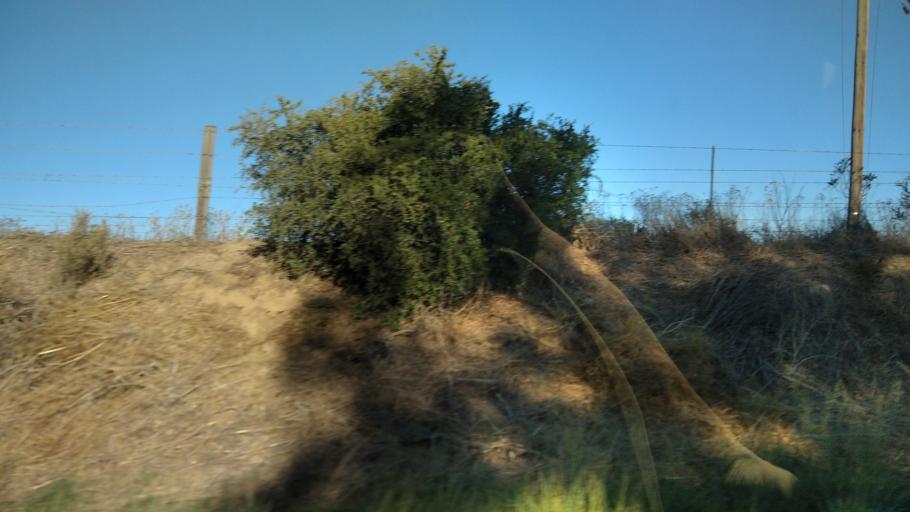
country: ZA
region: Western Cape
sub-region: West Coast District Municipality
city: Malmesbury
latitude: -33.3913
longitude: 18.6722
